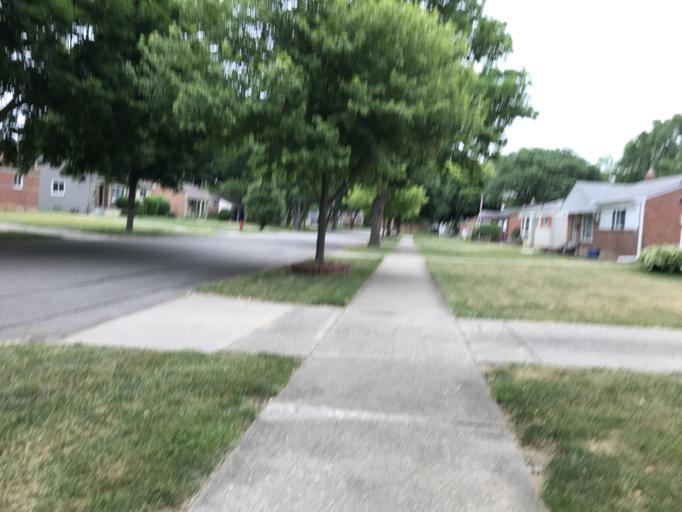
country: US
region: Michigan
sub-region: Oakland County
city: Farmington
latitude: 42.4670
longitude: -83.3595
